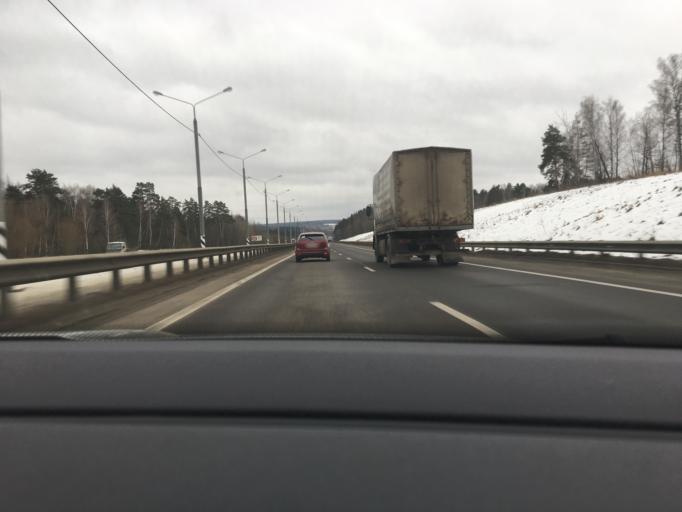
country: RU
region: Tula
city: Zaokskiy
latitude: 54.7901
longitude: 37.4868
